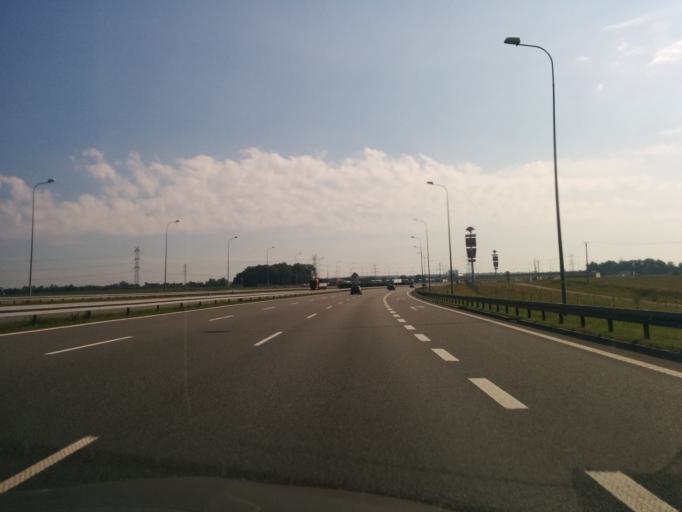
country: PL
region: Silesian Voivodeship
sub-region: Powiat tarnogorski
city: Wieszowa
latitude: 50.3685
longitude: 18.7352
